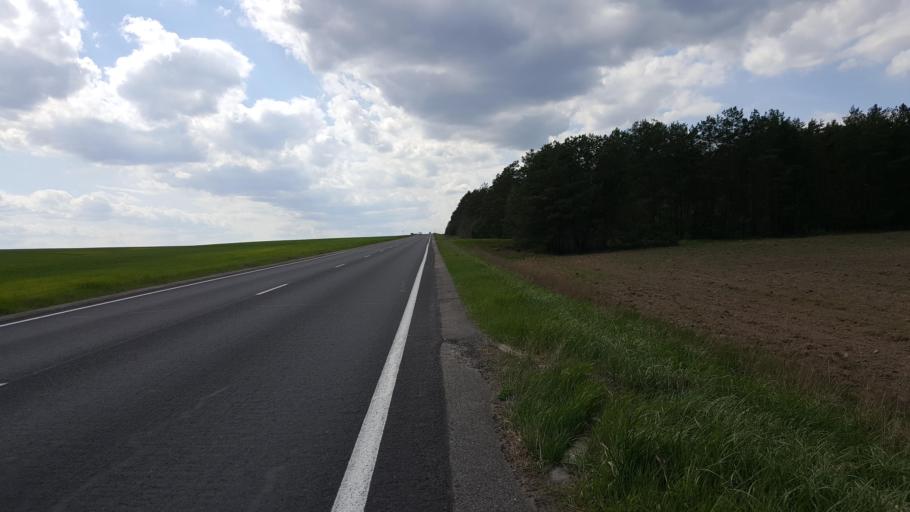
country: BY
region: Brest
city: Kamyanyets
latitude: 52.3928
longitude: 23.9630
